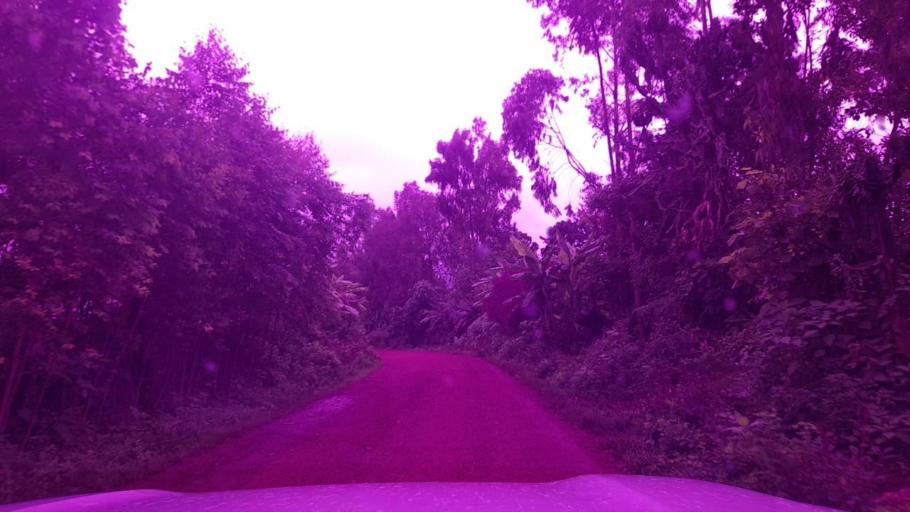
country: ET
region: Southern Nations, Nationalities, and People's Region
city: Bonga
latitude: 7.5897
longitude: 36.0162
